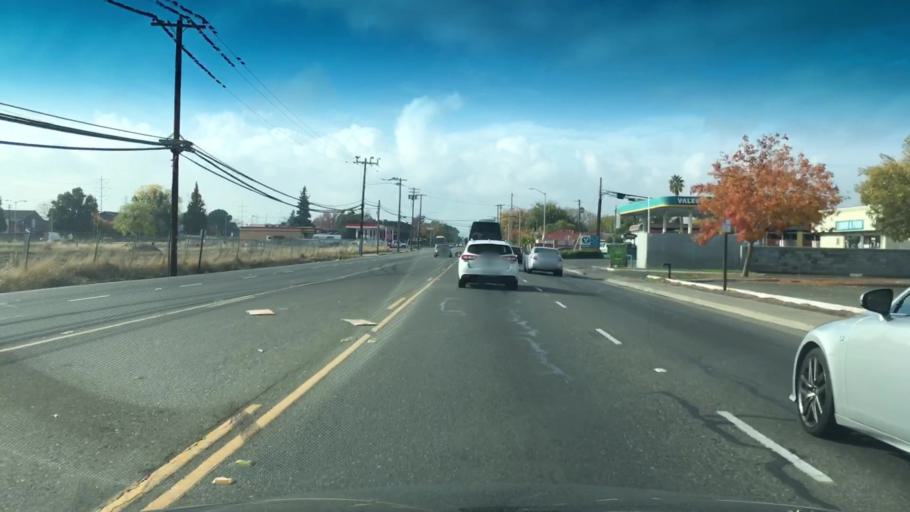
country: US
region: California
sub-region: Sacramento County
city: Parkway
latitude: 38.5105
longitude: -121.4477
